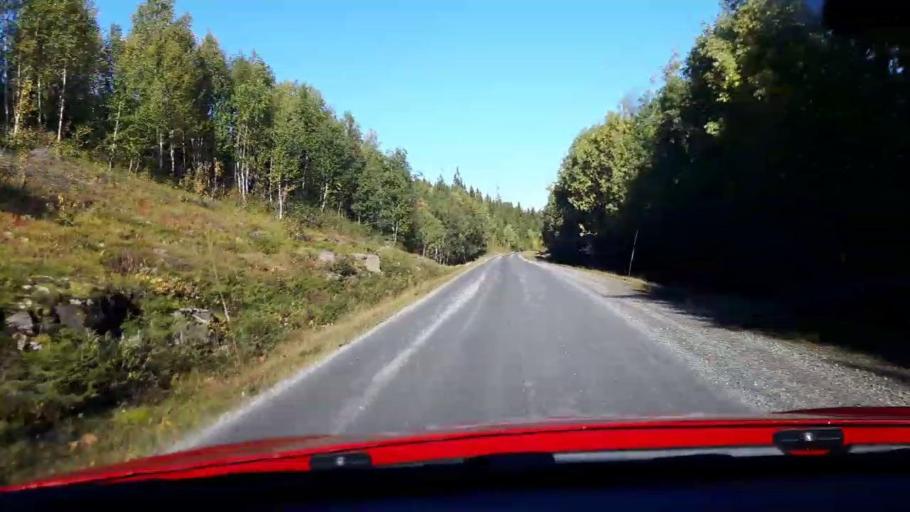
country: NO
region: Nord-Trondelag
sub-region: Lierne
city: Sandvika
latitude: 64.5736
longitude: 13.9003
